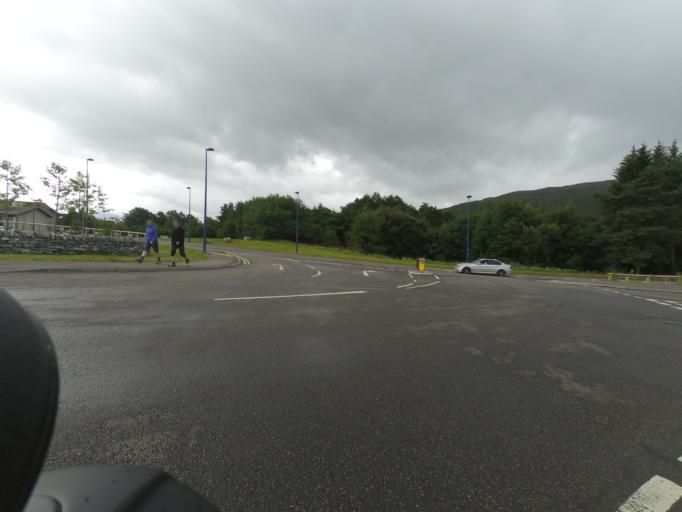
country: GB
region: Scotland
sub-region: Highland
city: Aviemore
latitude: 57.1922
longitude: -3.8306
